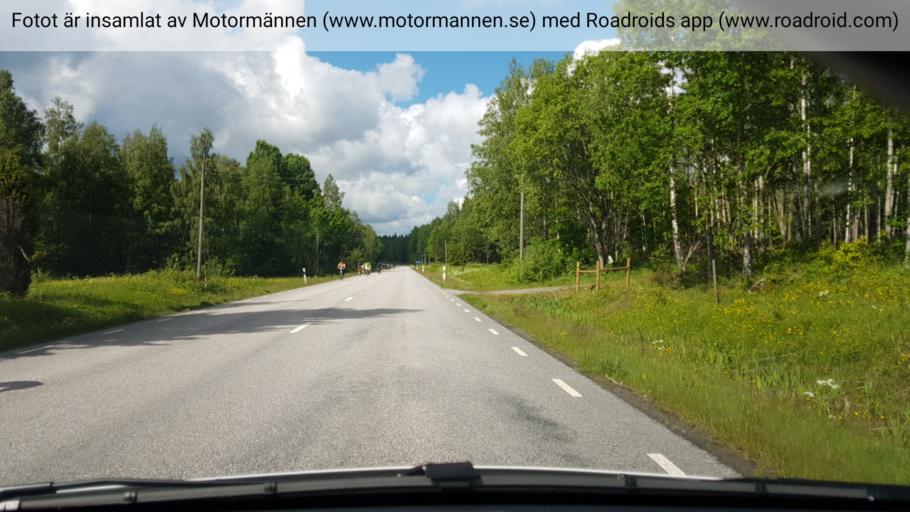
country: SE
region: Vaestra Goetaland
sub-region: Karlsborgs Kommun
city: Karlsborg
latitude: 58.6970
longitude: 14.6958
